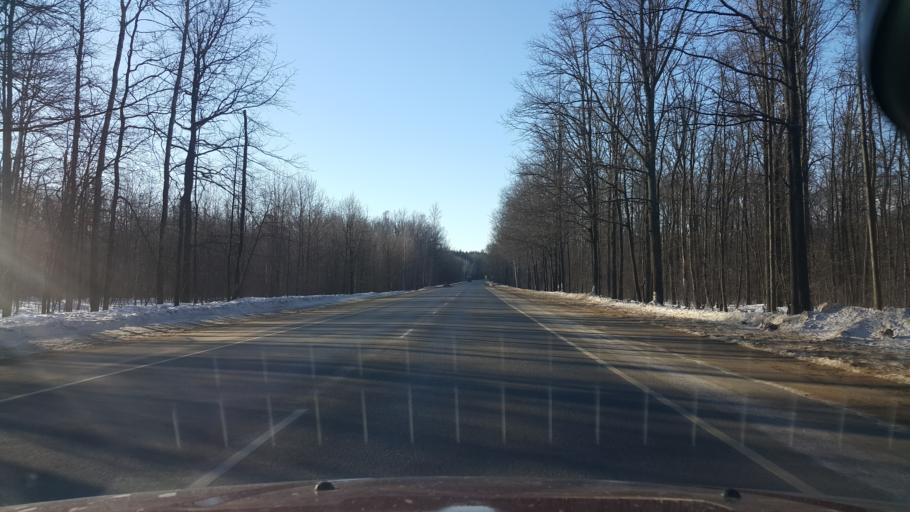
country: RU
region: Tambov
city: Novaya Lyada
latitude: 52.6965
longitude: 41.5471
